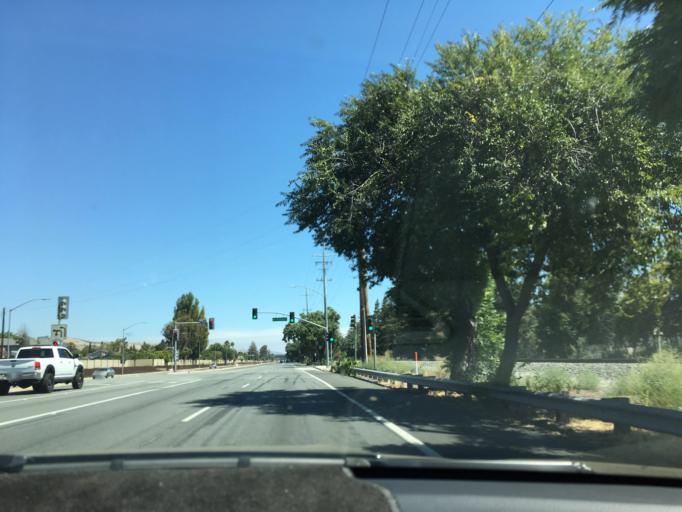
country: US
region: California
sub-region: Santa Clara County
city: Seven Trees
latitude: 37.2478
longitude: -121.7896
